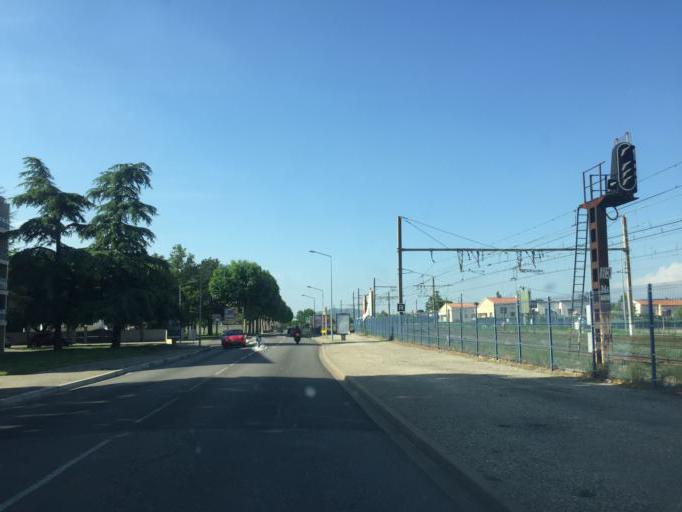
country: FR
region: Rhone-Alpes
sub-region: Departement de la Drome
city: Pierrelatte
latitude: 44.3785
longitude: 4.7043
